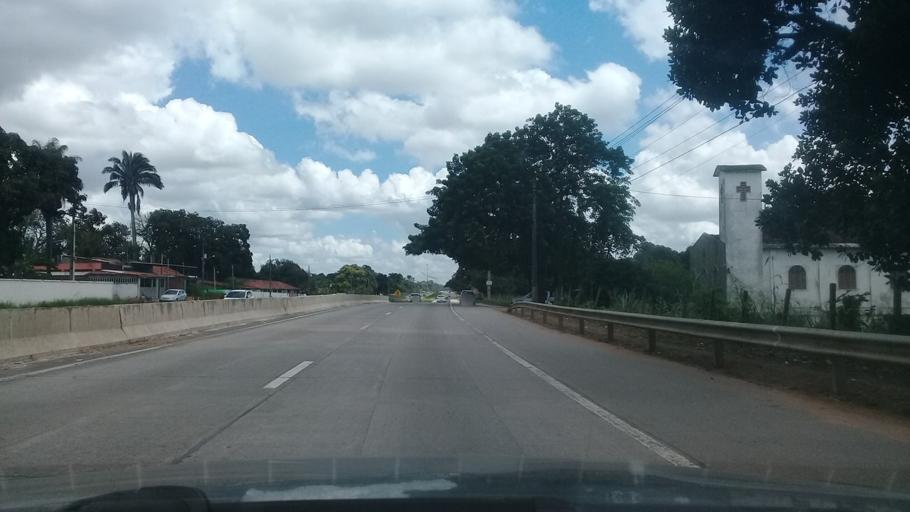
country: BR
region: Pernambuco
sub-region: Sao Lourenco Da Mata
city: Sao Lourenco da Mata
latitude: -7.9324
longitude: -35.1352
